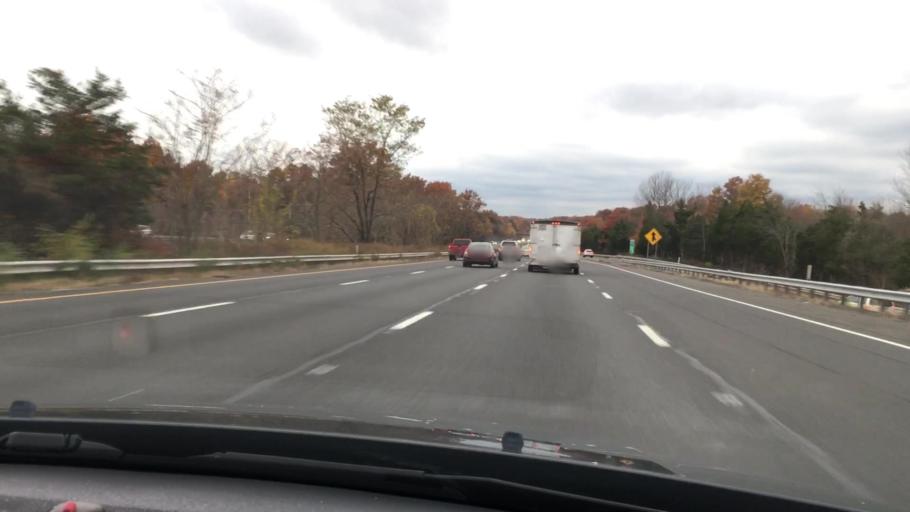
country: US
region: New Jersey
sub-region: Somerset County
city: Bernardsville
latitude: 40.6890
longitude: -74.5782
